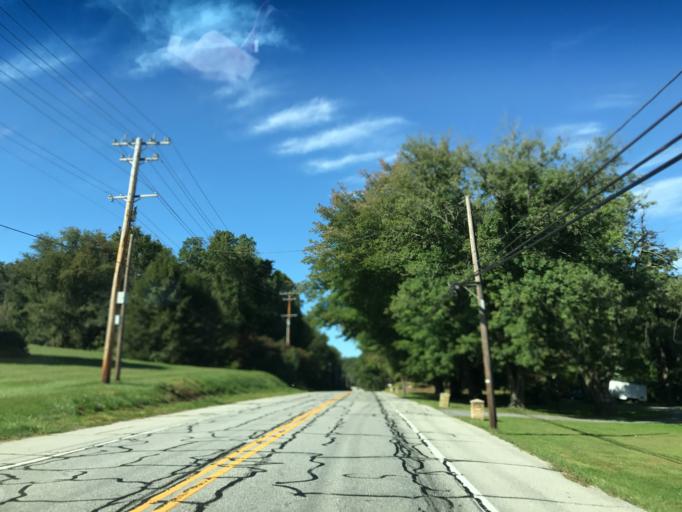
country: US
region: Maryland
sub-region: Anne Arundel County
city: Davidsonville
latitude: 38.9167
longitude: -76.6443
